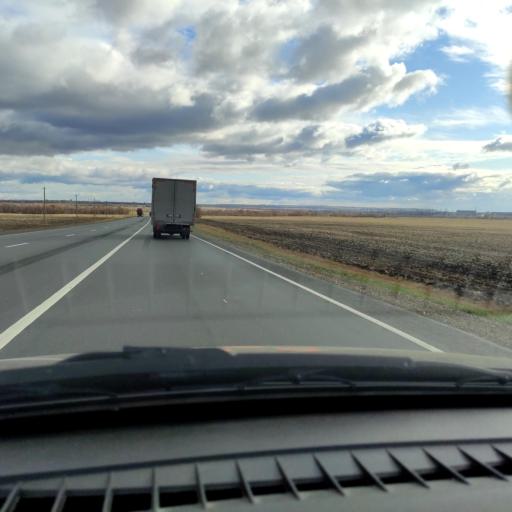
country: RU
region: Samara
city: Varlamovo
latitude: 53.2114
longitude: 48.4567
